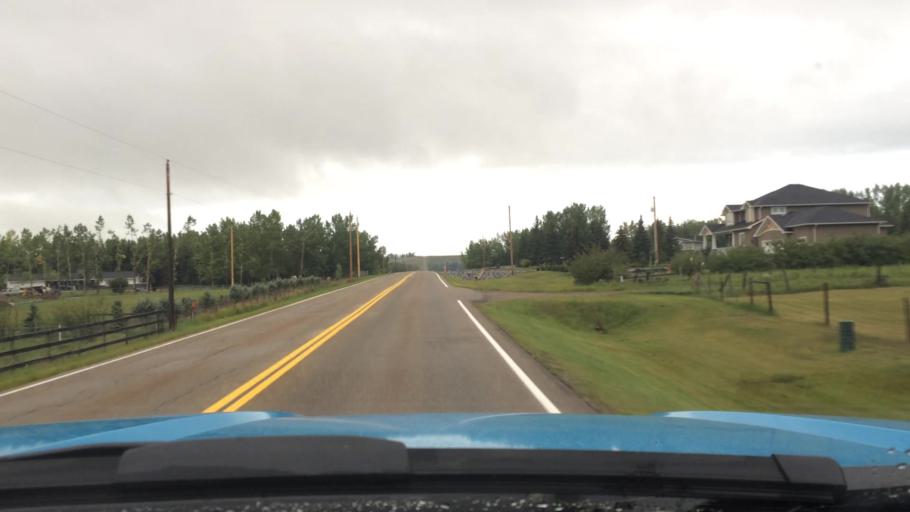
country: CA
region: Alberta
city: Airdrie
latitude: 51.2046
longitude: -114.1412
